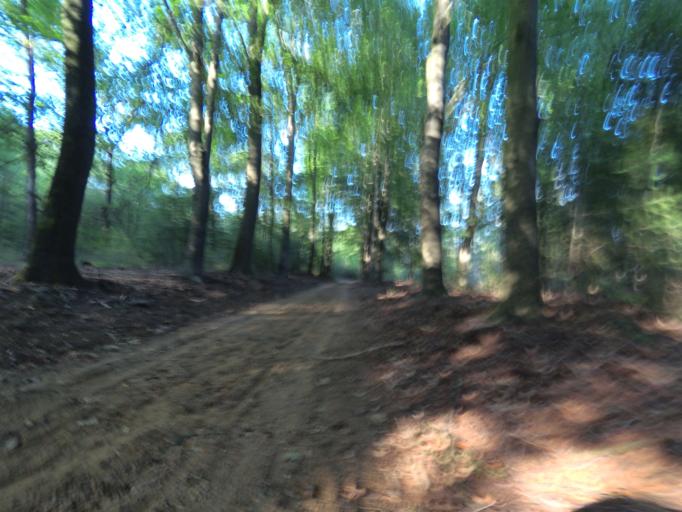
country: NL
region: Gelderland
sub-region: Gemeente Apeldoorn
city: Beekbergen
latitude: 52.1561
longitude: 5.9290
